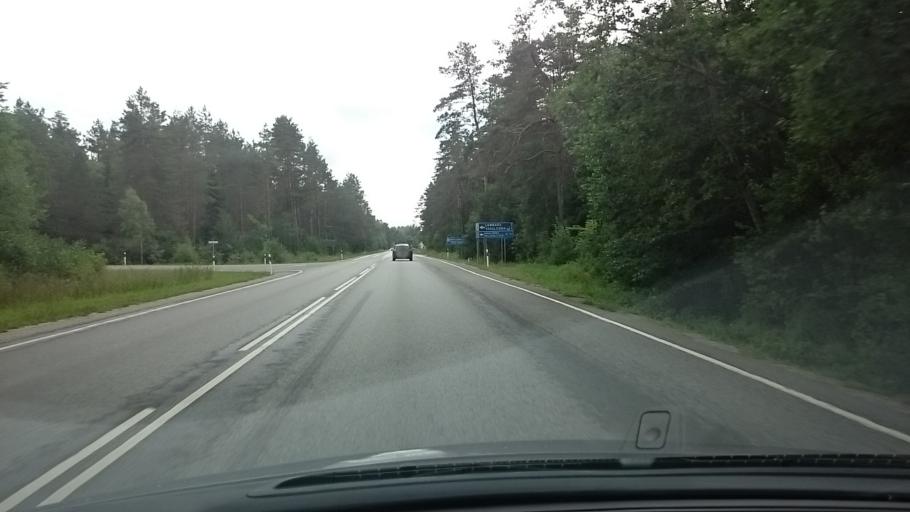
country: EE
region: Harju
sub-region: Nissi vald
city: Riisipere
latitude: 59.2446
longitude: 24.2783
